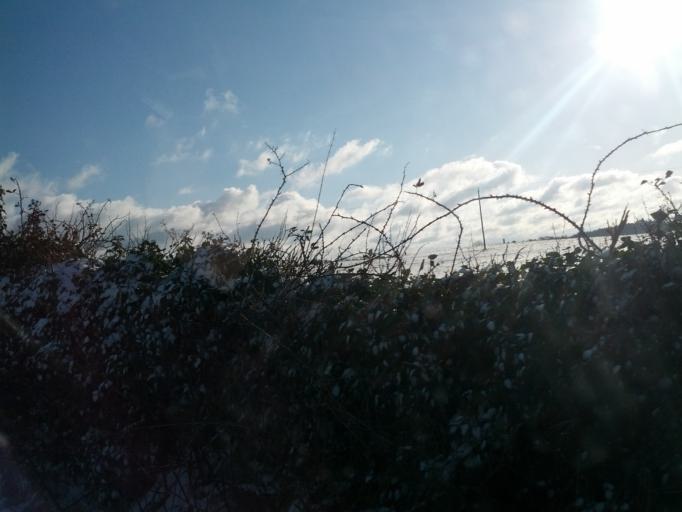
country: IE
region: Connaught
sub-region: County Galway
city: Athenry
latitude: 53.1928
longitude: -8.7932
